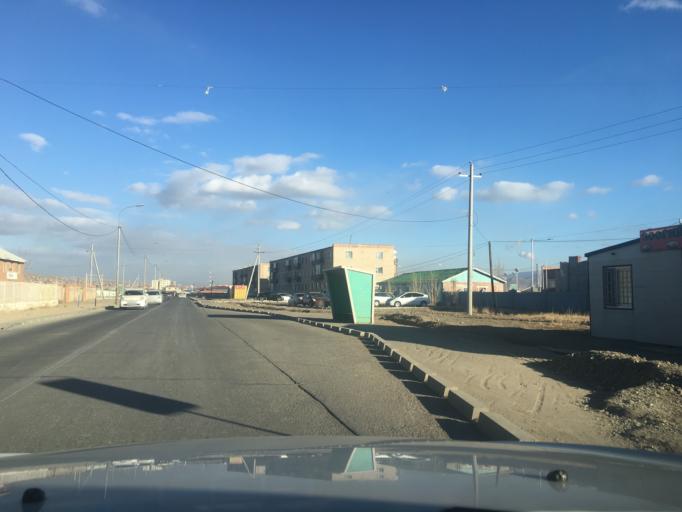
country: MN
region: Ulaanbaatar
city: Ulaanbaatar
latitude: 47.9118
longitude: 106.7394
